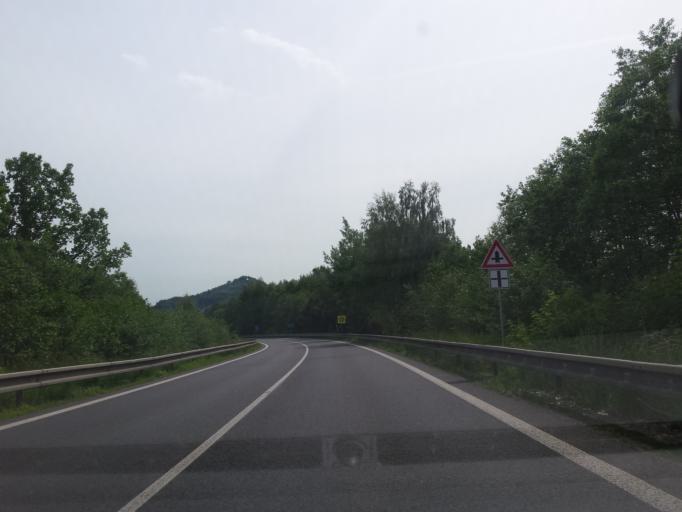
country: CZ
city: Novy Bor
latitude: 50.7580
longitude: 14.5343
